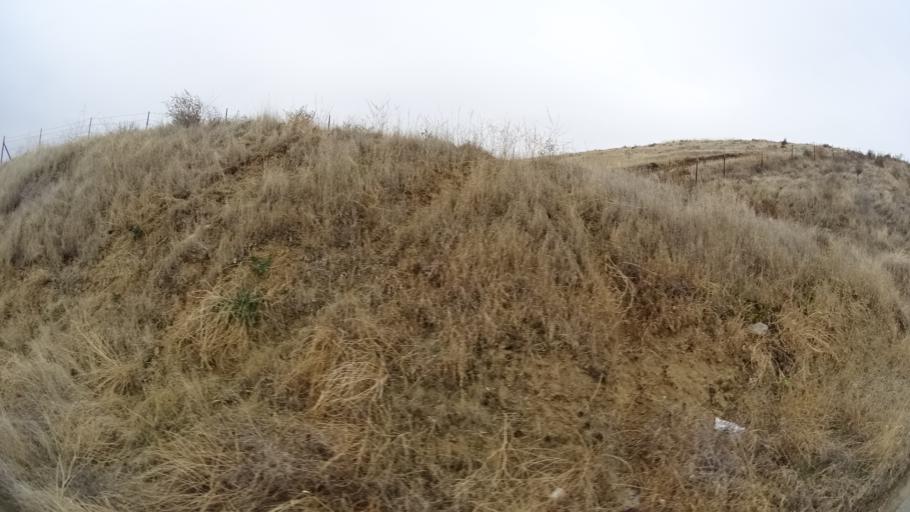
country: US
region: California
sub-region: Kern County
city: Oildale
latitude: 35.4241
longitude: -118.9439
